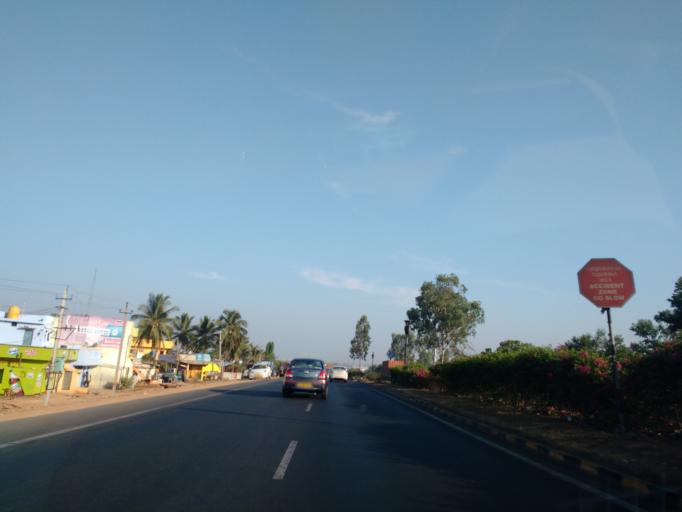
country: IN
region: Karnataka
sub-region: Bangalore Rural
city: Nelamangala
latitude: 13.1207
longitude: 77.3687
